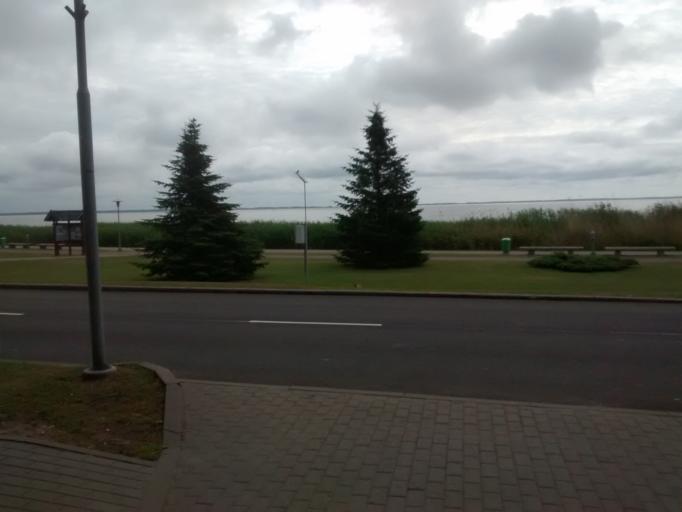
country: LT
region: Klaipedos apskritis
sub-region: Klaipeda
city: Klaipeda
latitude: 55.5408
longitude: 21.1198
